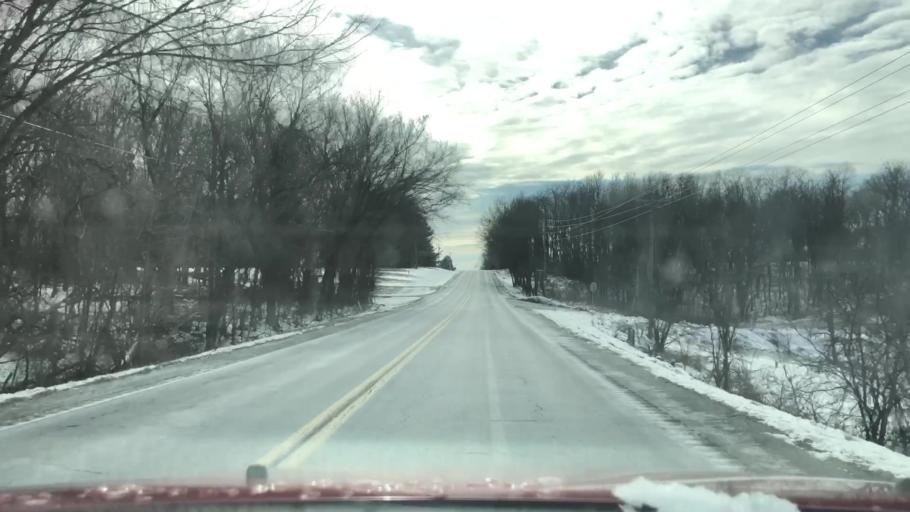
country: US
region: Missouri
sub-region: Jackson County
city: Lone Jack
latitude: 38.8858
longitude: -94.1347
